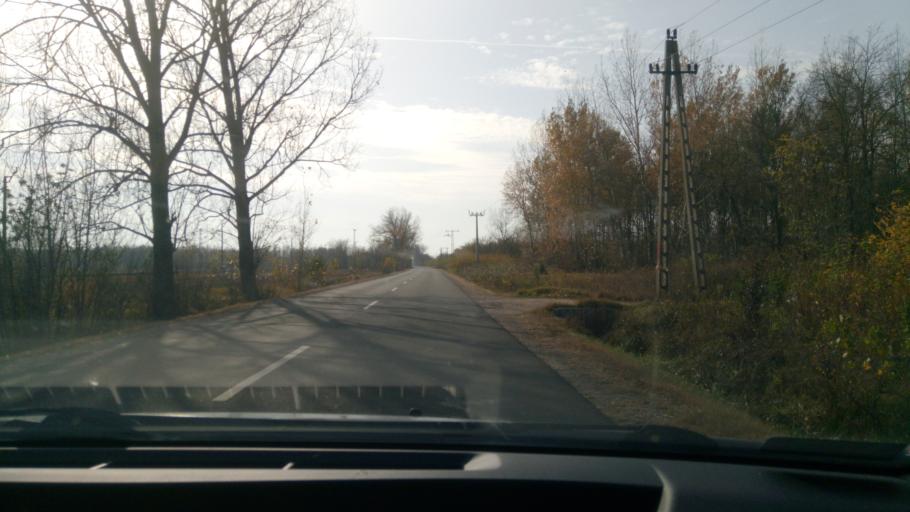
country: HU
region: Bacs-Kiskun
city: Jaszszentlaszlo
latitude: 46.6160
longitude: 19.7965
